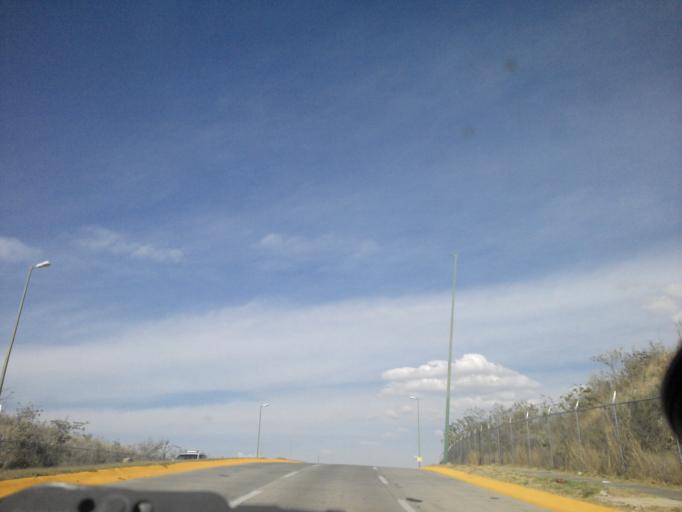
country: MX
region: Jalisco
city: Guadalajara
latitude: 20.6735
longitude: -103.4588
